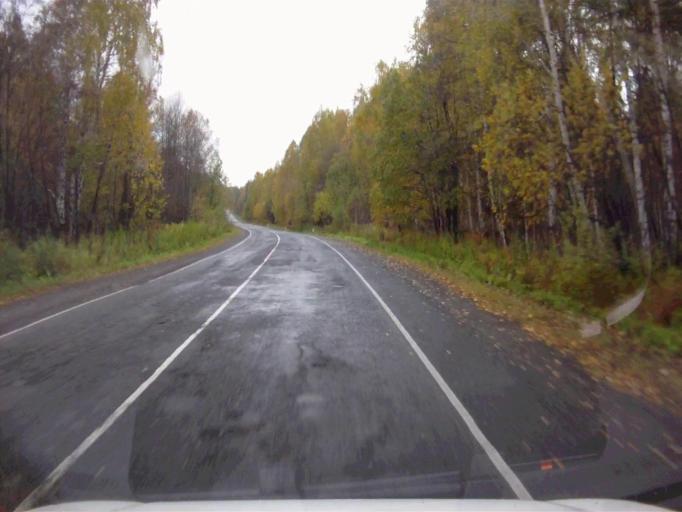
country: RU
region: Chelyabinsk
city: Nizhniy Ufaley
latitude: 56.0548
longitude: 60.0513
